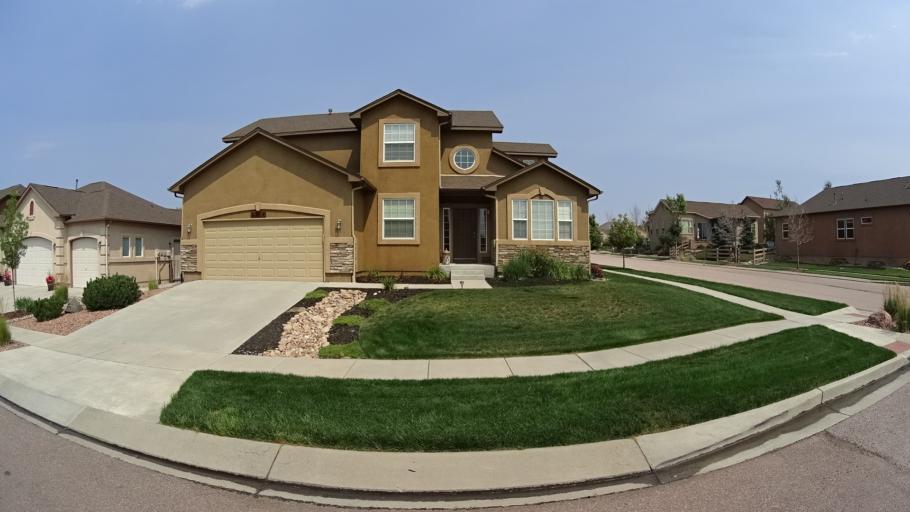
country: US
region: Colorado
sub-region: El Paso County
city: Black Forest
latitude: 38.9658
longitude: -104.7192
